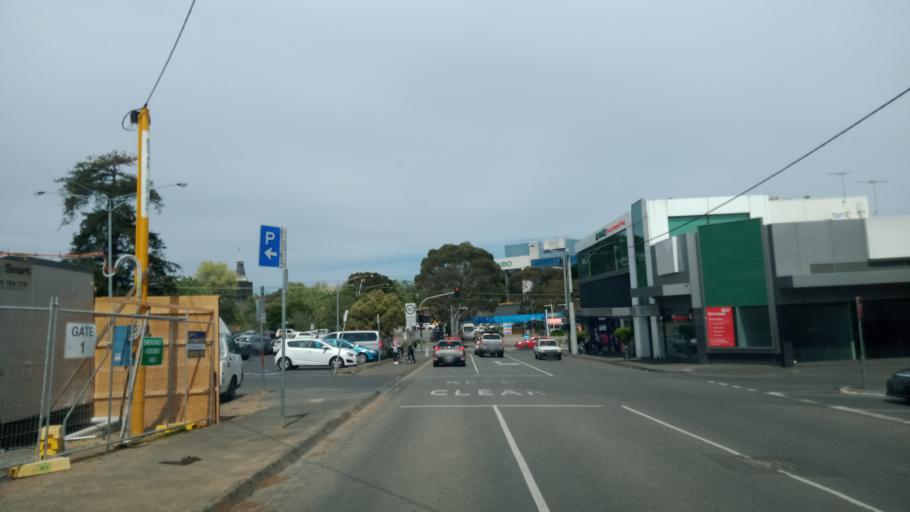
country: AU
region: Victoria
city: Glenferrie
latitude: -37.8310
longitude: 145.0592
